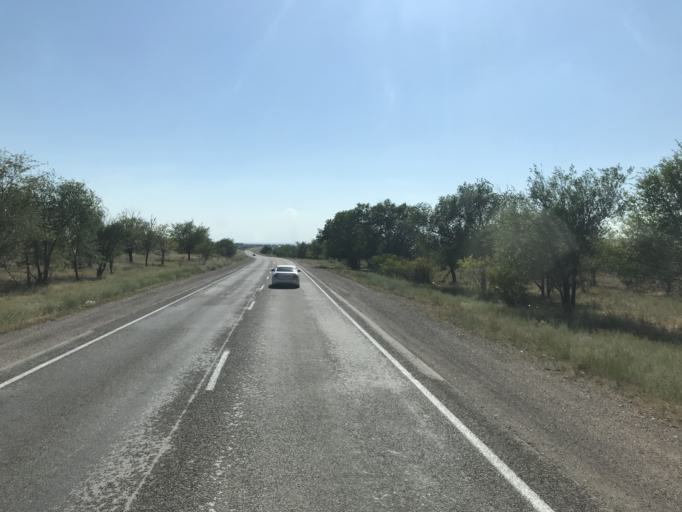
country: KZ
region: Zhambyl
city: Georgiyevka
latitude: 43.2476
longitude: 74.7924
